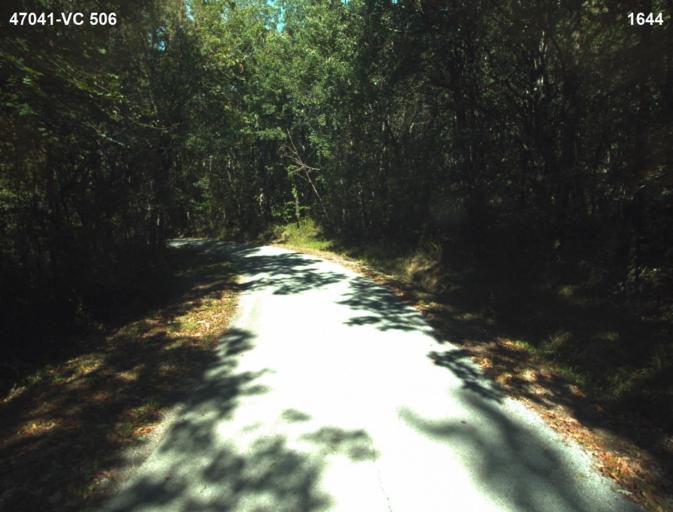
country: FR
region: Aquitaine
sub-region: Departement du Lot-et-Garonne
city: Port-Sainte-Marie
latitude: 44.2017
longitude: 0.3861
